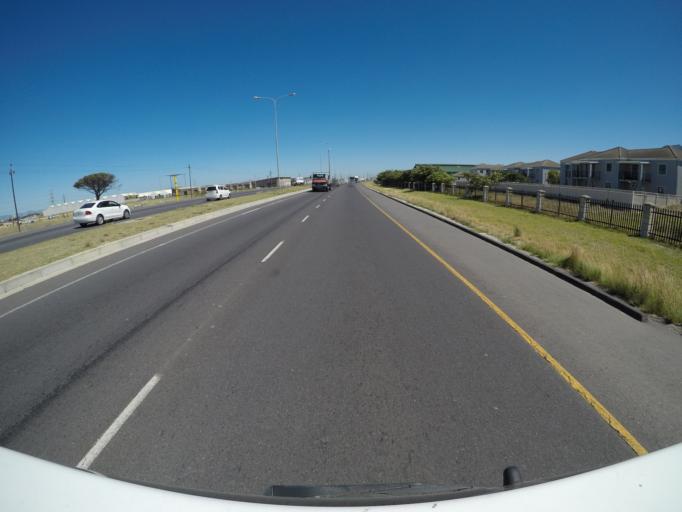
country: ZA
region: Western Cape
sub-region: Overberg District Municipality
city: Grabouw
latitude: -34.1064
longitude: 18.8582
